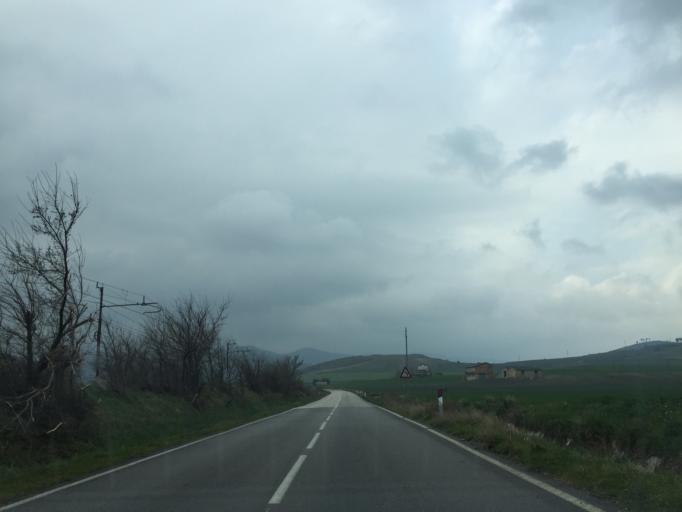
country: IT
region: Apulia
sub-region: Provincia di Foggia
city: Bovino
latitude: 41.2915
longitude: 15.3822
